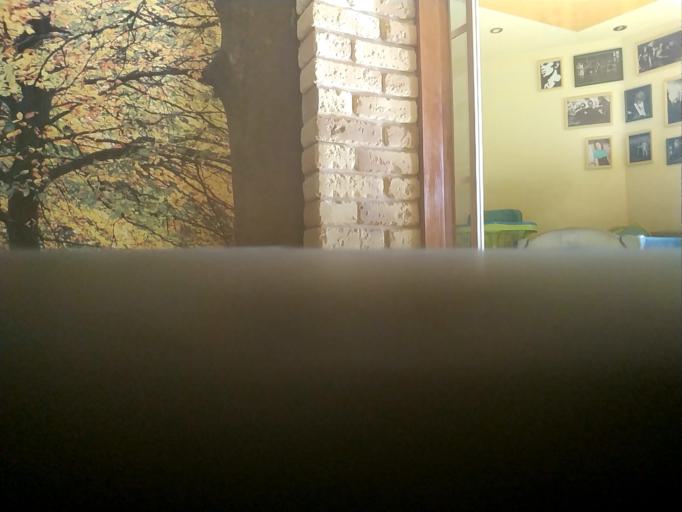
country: RU
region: Smolensk
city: Temkino
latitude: 55.0053
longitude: 34.9356
